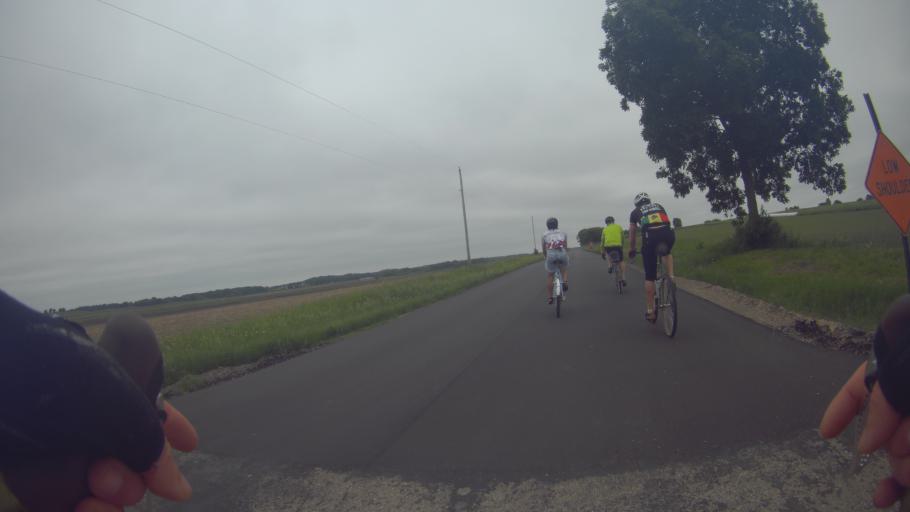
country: US
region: Wisconsin
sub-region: Green County
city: Brooklyn
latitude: 42.8706
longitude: -89.4116
